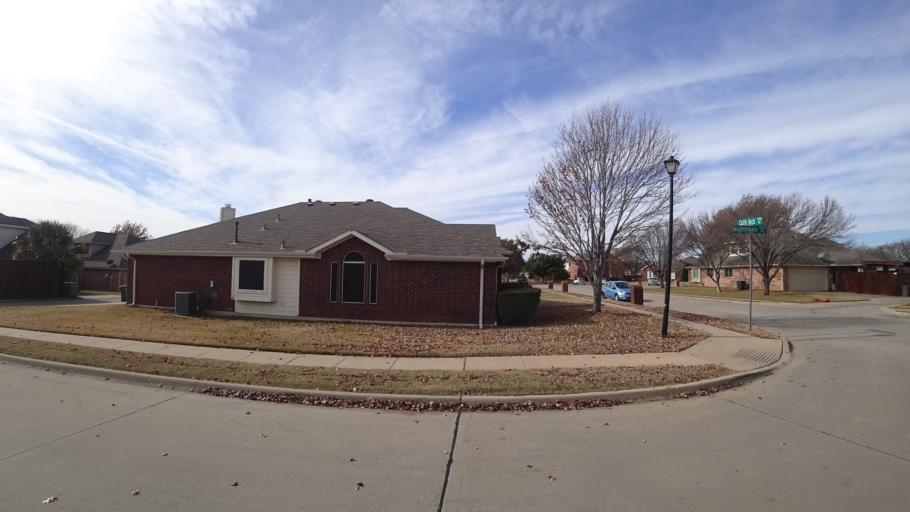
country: US
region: Texas
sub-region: Denton County
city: Highland Village
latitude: 33.0679
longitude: -97.0390
